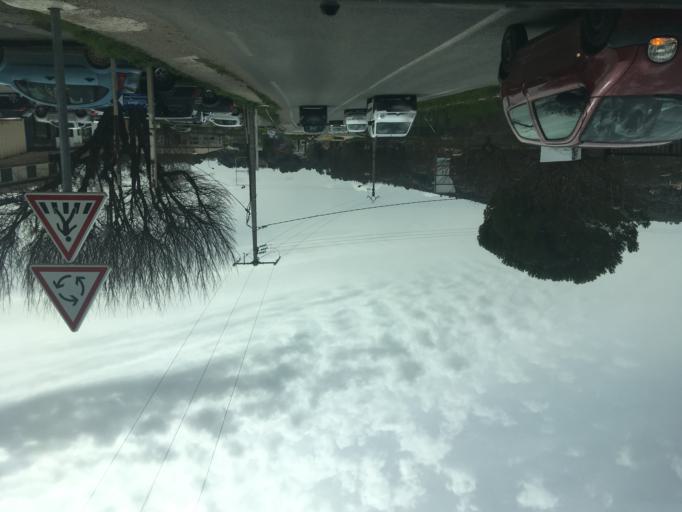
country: FR
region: Provence-Alpes-Cote d'Azur
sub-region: Departement du Var
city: Montauroux
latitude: 43.6025
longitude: 6.7768
